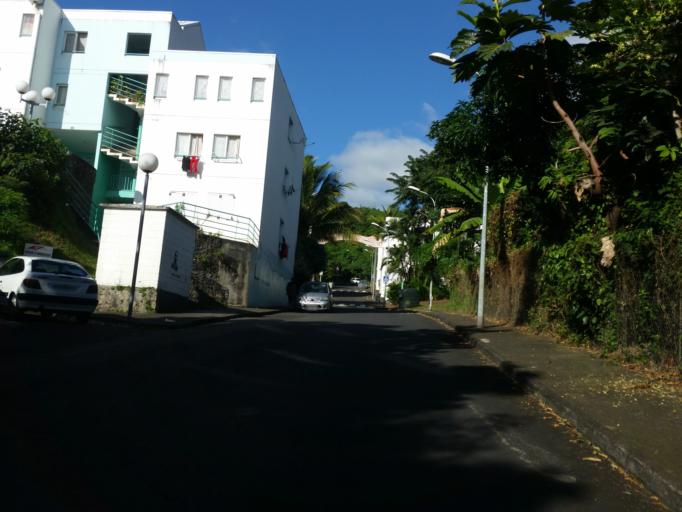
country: RE
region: Reunion
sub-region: Reunion
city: Sainte-Marie
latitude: -20.9158
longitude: 55.5064
